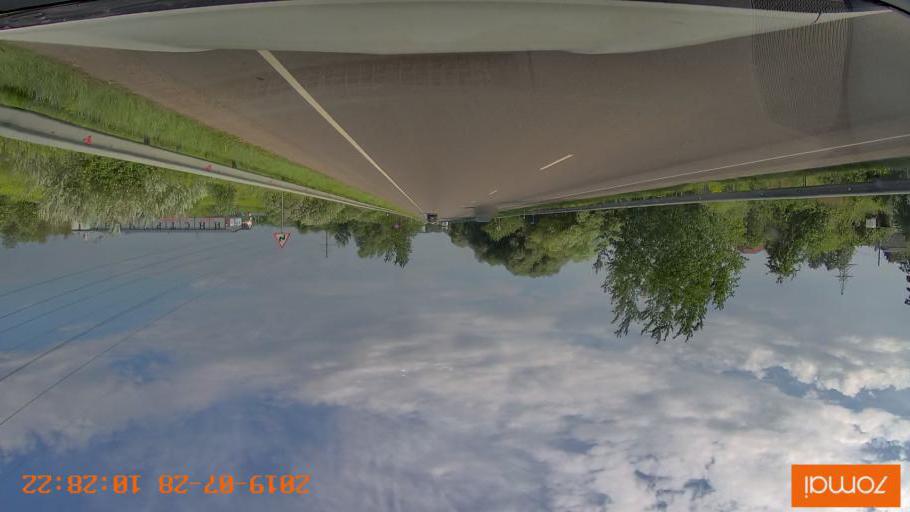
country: RU
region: Kaliningrad
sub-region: Gorod Kaliningrad
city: Kaliningrad
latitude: 54.7696
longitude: 20.5002
